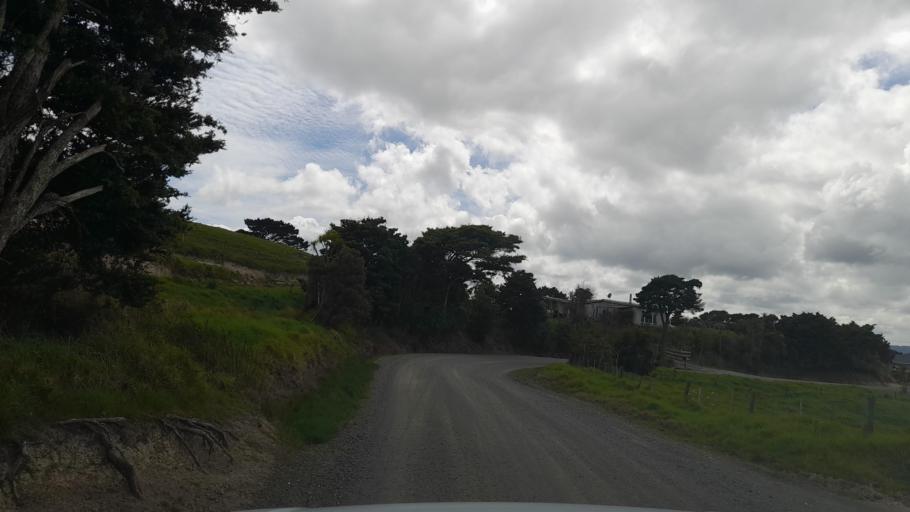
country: NZ
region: Auckland
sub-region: Auckland
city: Wellsford
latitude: -36.2019
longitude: 174.3366
